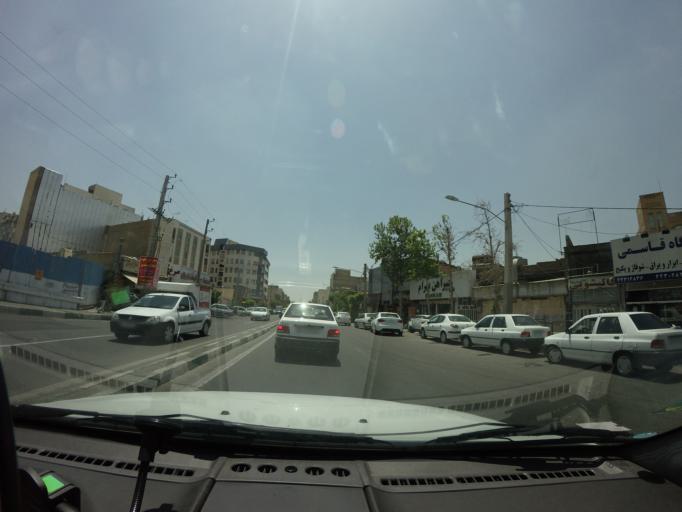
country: IR
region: Tehran
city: Tajrish
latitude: 35.7630
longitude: 51.2841
